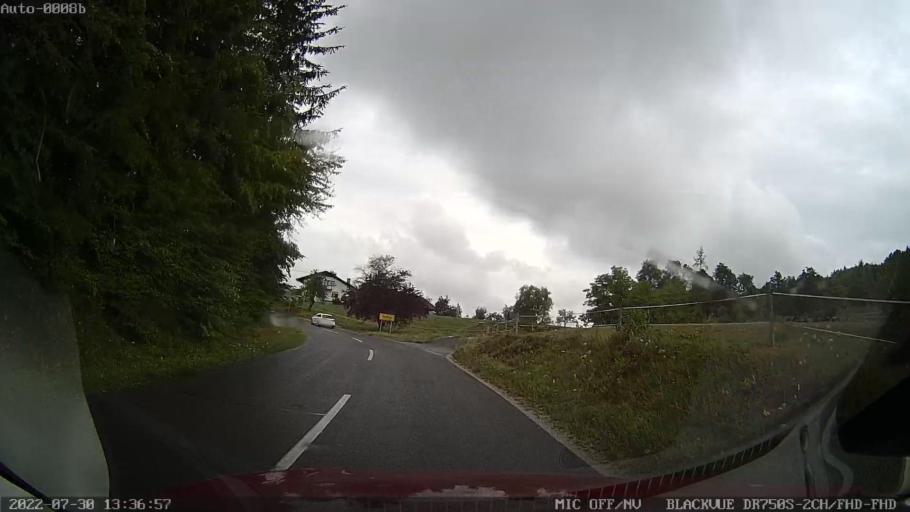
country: SI
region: Zuzemberk
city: Zuzemberk
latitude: 45.8737
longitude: 14.9205
